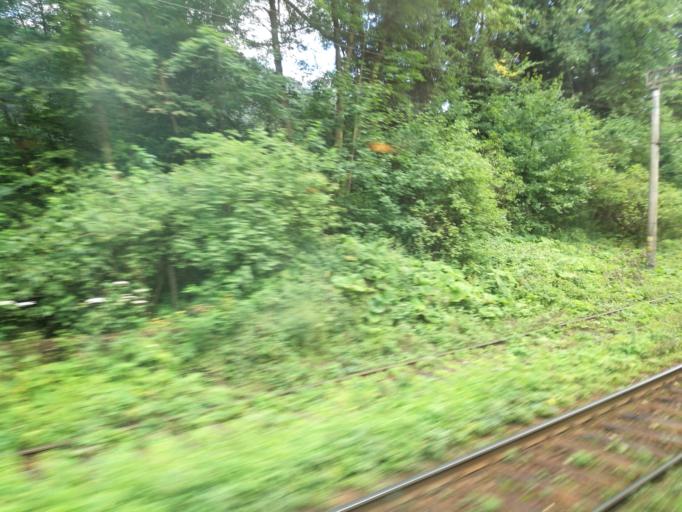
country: RO
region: Brasov
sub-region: Oras Predeal
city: Predeal
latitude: 45.5525
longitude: 25.5883
